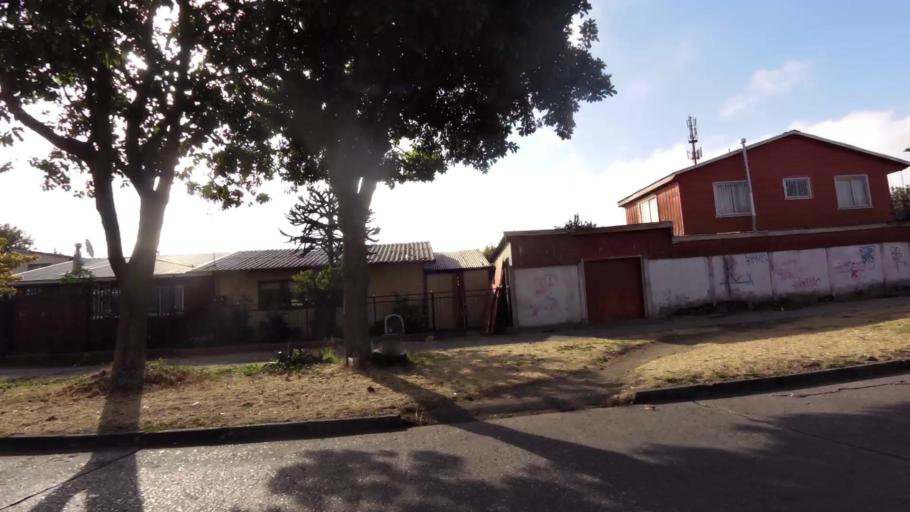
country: CL
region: Biobio
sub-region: Provincia de Concepcion
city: Concepcion
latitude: -36.7918
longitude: -73.1036
